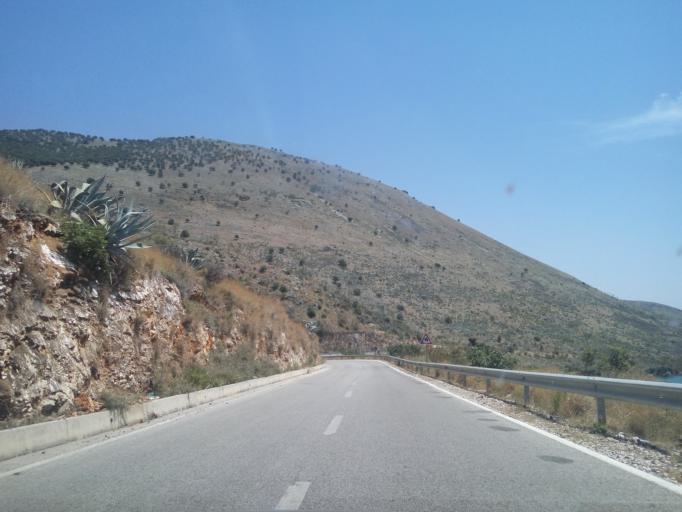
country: AL
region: Vlore
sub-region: Rrethi i Vlores
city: Himare
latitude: 40.0698
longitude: 19.7875
